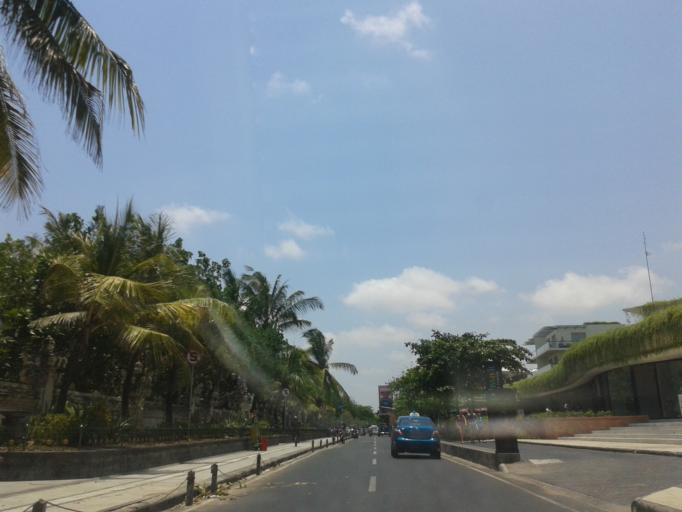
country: ID
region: Bali
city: Kuta
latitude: -8.7183
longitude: 115.1690
